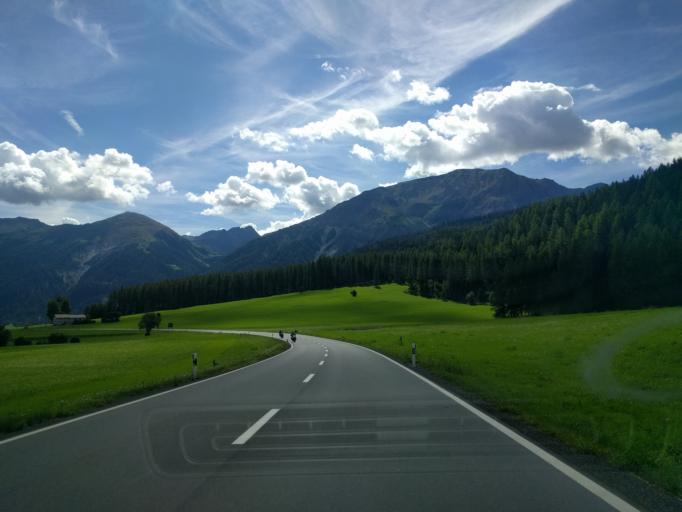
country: IT
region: Trentino-Alto Adige
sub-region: Bolzano
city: Tubre
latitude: 46.6071
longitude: 10.3752
